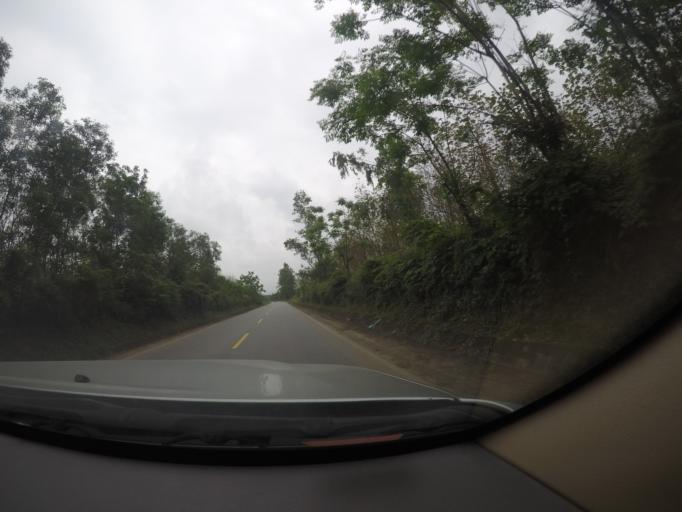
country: VN
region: Quang Binh
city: Hoan Lao
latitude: 17.5416
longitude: 106.4665
